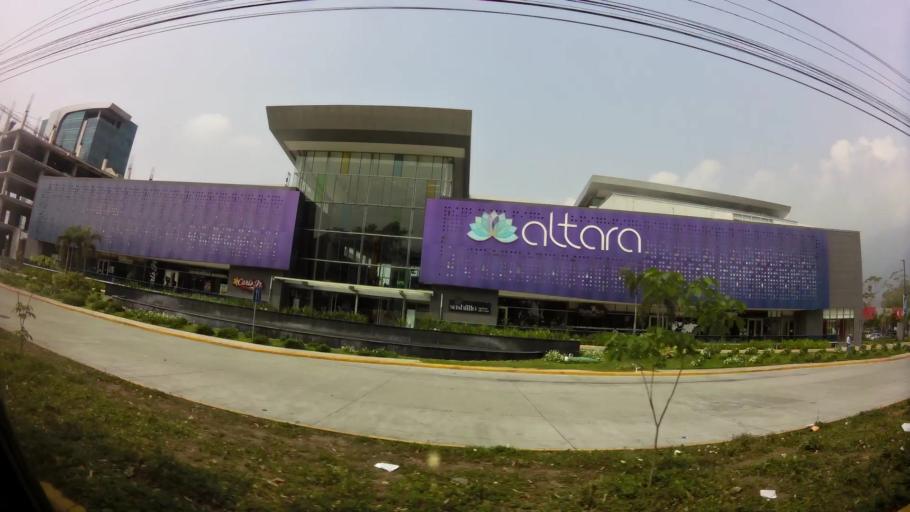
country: HN
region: Cortes
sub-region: San Pedro Sula
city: Pena Blanca
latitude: 15.5633
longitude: -88.0213
